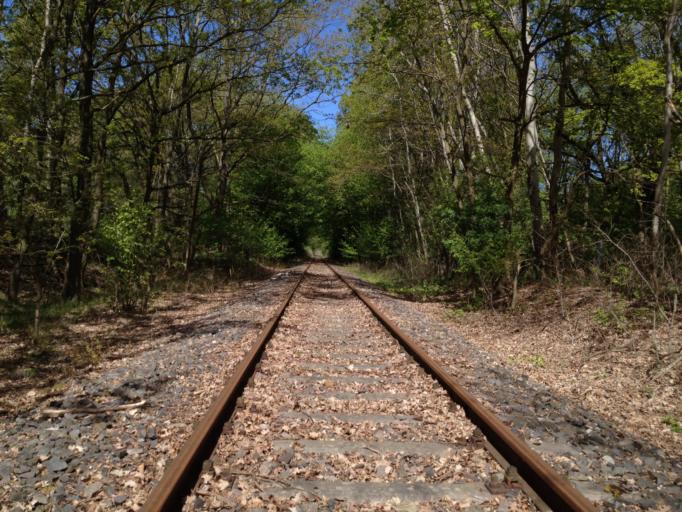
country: DE
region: Brandenburg
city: Templin
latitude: 53.1267
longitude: 13.4441
